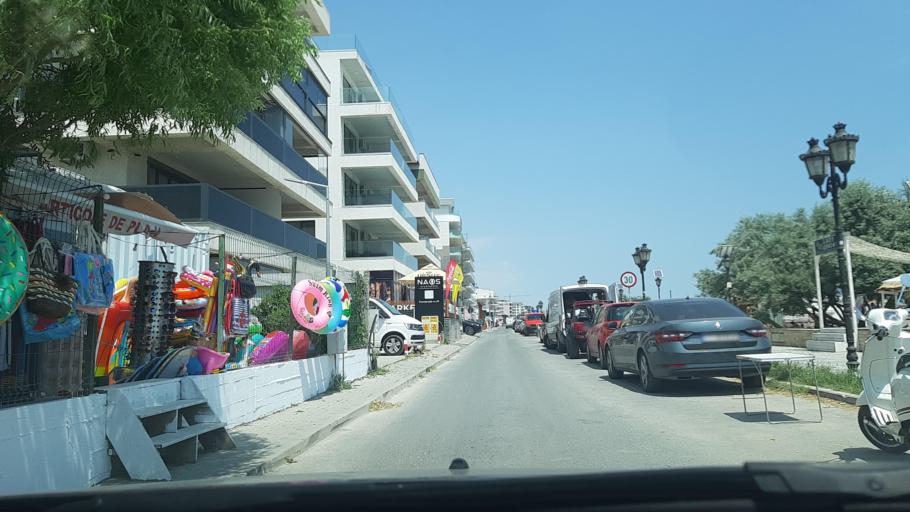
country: RO
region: Constanta
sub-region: Comuna Navodari
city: Navodari
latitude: 44.2974
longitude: 28.6252
